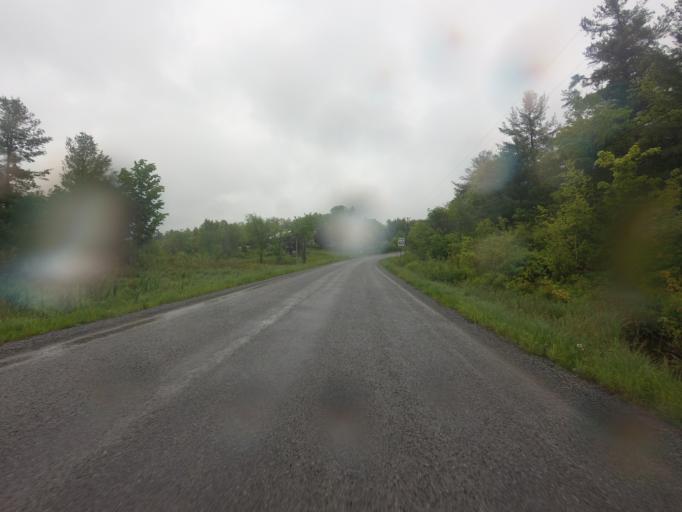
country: CA
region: Ontario
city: Kingston
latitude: 44.4821
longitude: -76.4651
